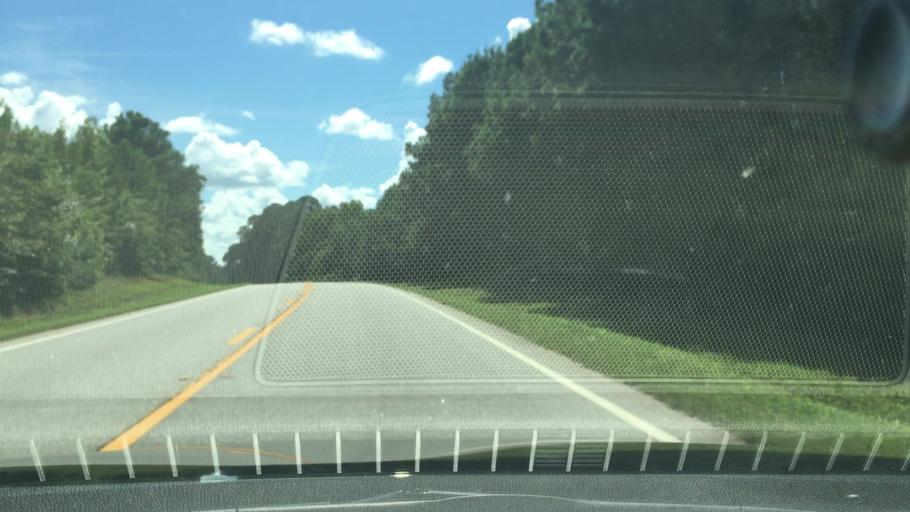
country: US
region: Georgia
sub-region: Jasper County
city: Monticello
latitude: 33.3144
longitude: -83.7608
